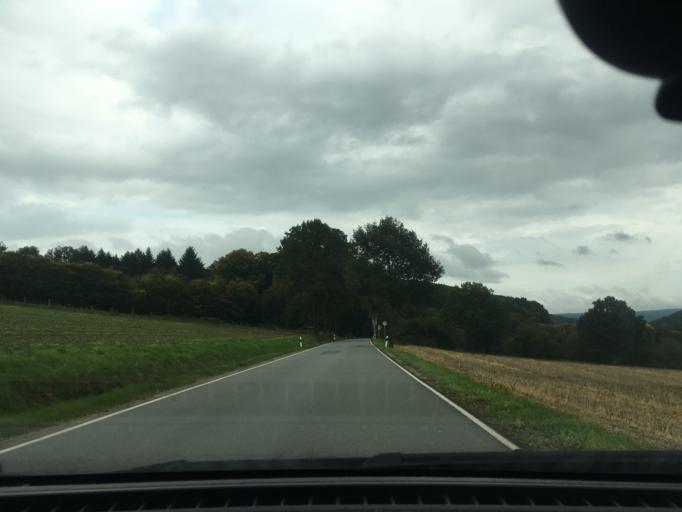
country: DE
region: Lower Saxony
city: Bodenfelde
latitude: 51.6887
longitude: 9.5220
